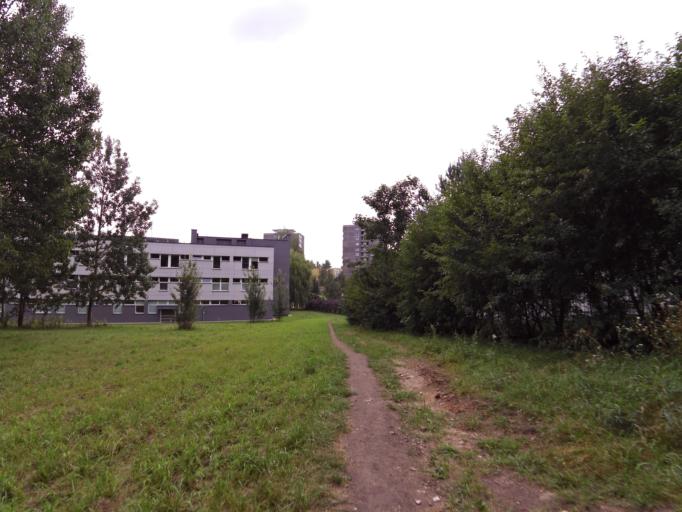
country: LT
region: Vilnius County
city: Lazdynai
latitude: 54.6777
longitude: 25.2074
